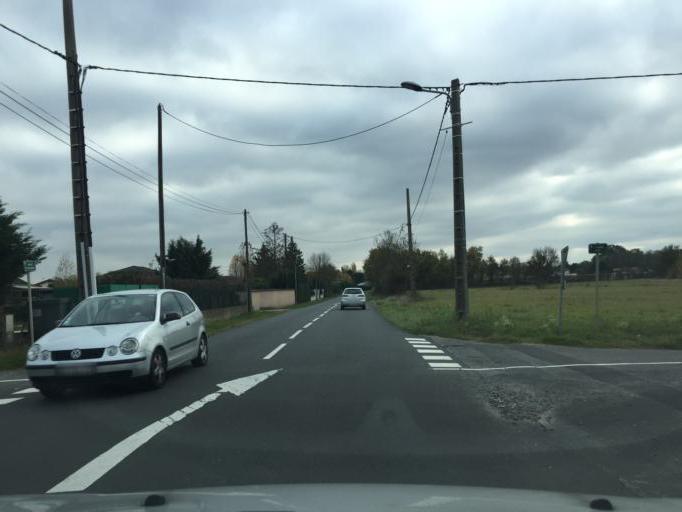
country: FR
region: Rhone-Alpes
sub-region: Departement de l'Ain
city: Saint-Didier-de-Formans
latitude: 45.9529
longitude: 4.8056
